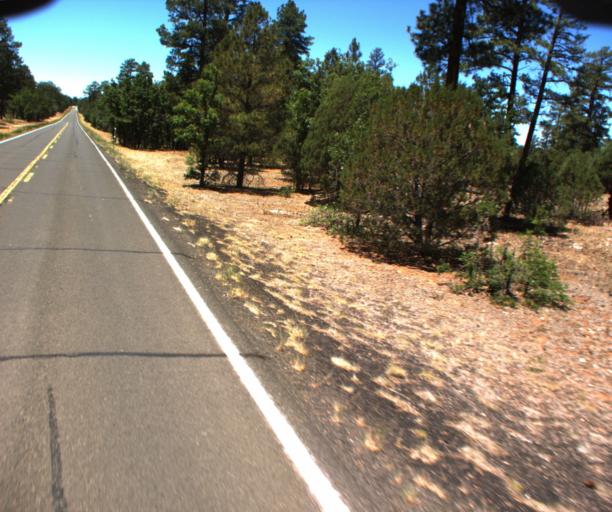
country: US
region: Arizona
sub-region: Gila County
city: Star Valley
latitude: 34.6265
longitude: -111.1428
